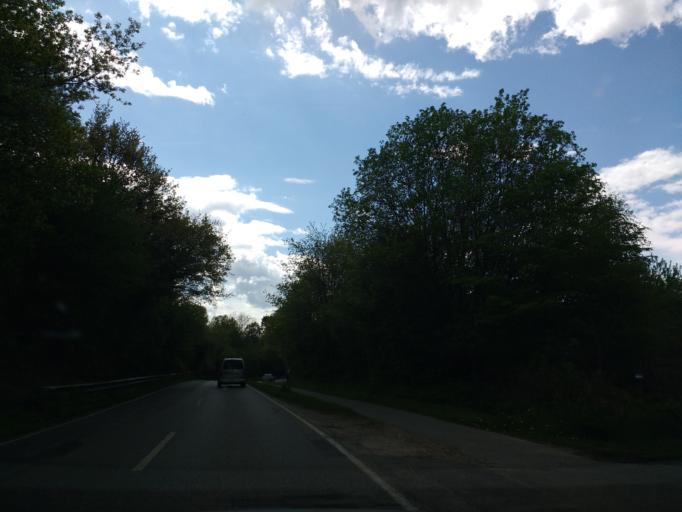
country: DE
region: Schleswig-Holstein
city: Eckernforde
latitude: 54.4865
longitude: 9.8567
